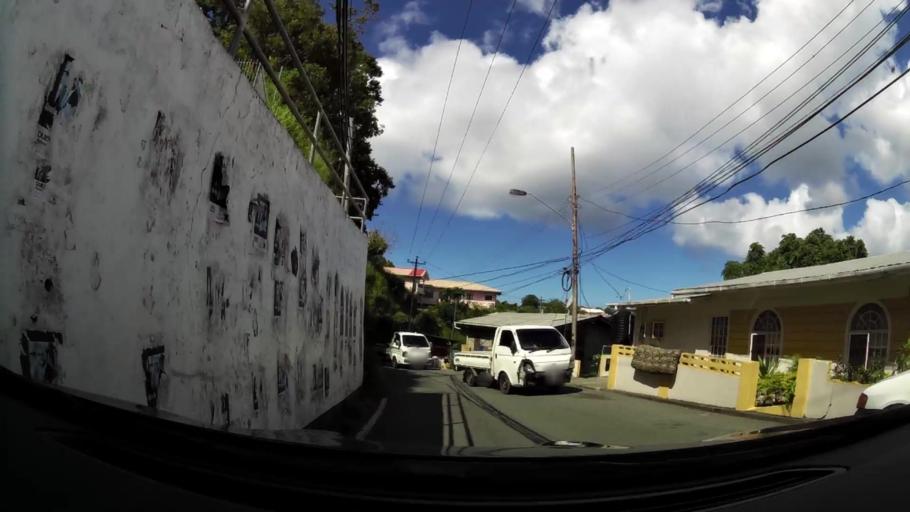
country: TT
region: Tobago
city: Scarborough
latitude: 11.2465
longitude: -60.7175
